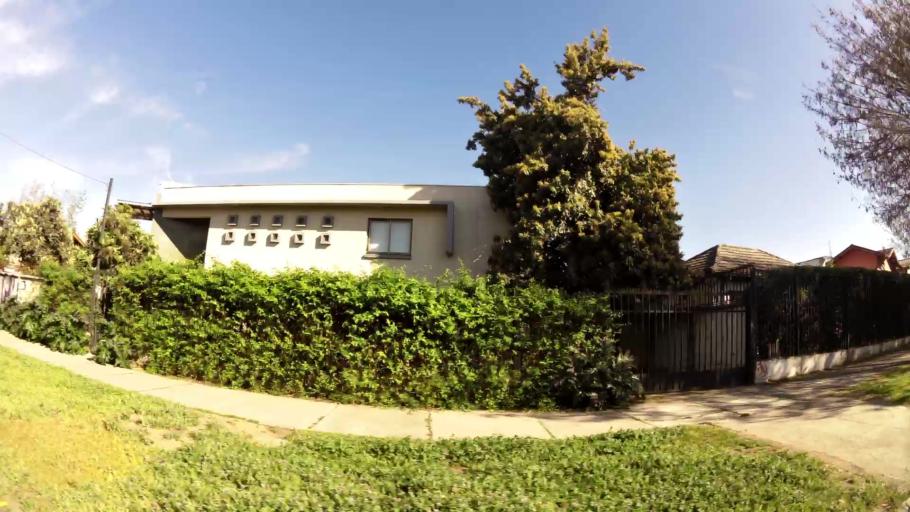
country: CL
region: Santiago Metropolitan
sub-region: Provincia de Santiago
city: Villa Presidente Frei, Nunoa, Santiago, Chile
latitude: -33.4356
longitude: -70.5551
